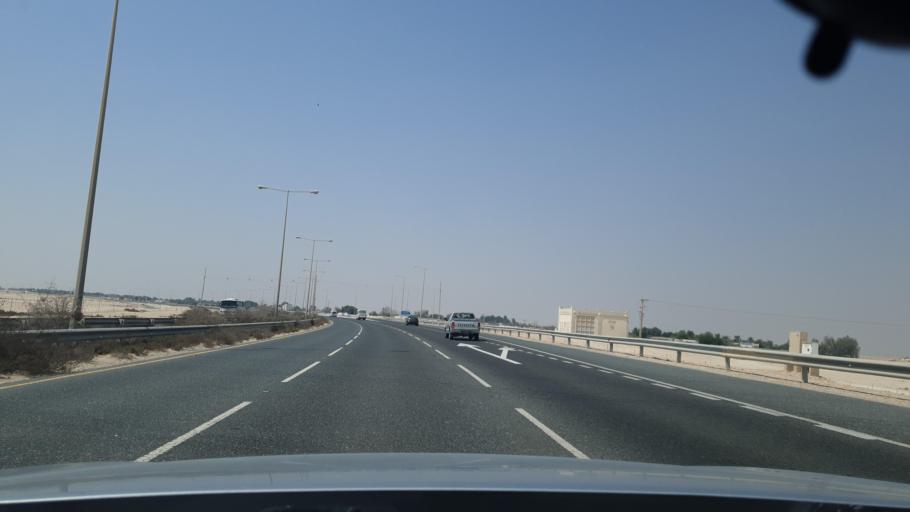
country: QA
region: Al Khawr
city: Al Khawr
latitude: 25.7568
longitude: 51.4718
